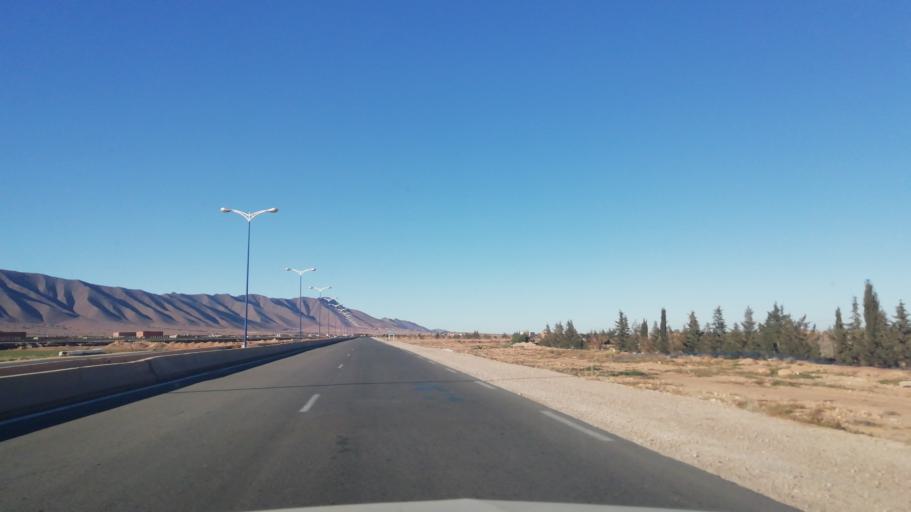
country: DZ
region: Wilaya de Naama
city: Naama
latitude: 33.5623
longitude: -0.2379
